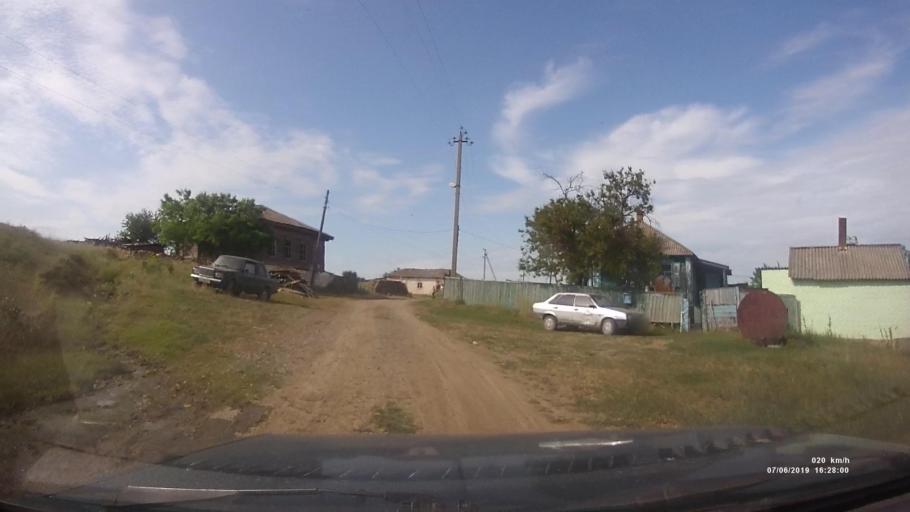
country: RU
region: Rostov
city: Staraya Stanitsa
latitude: 48.2541
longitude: 40.3189
